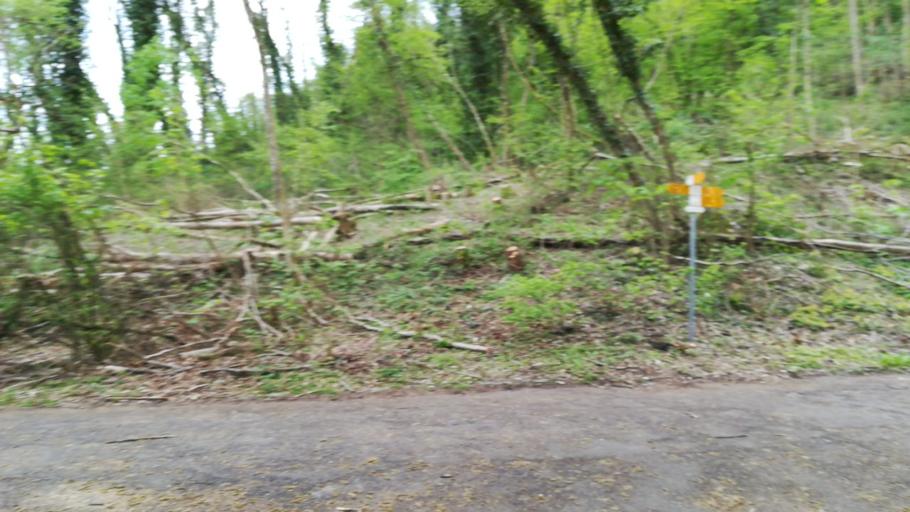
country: DE
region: Baden-Wuerttemberg
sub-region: Freiburg Region
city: Singen
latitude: 47.7662
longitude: 8.8235
